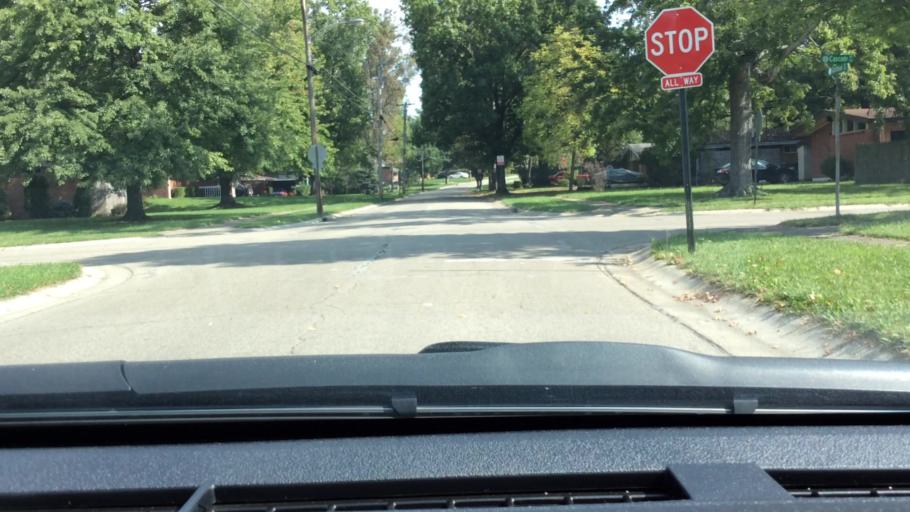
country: US
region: Ohio
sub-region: Hamilton County
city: Greenhills
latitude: 39.2704
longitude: -84.5077
